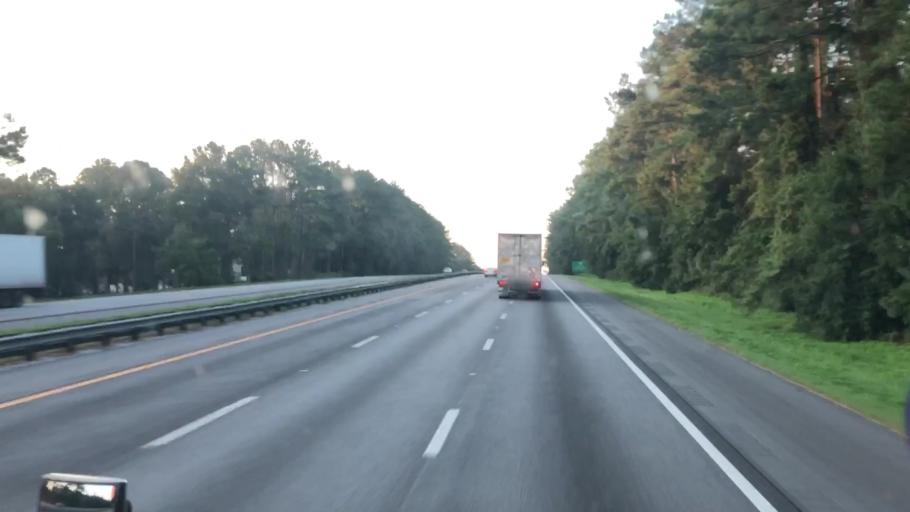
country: US
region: Florida
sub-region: Alachua County
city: High Springs
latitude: 29.8215
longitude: -82.5184
